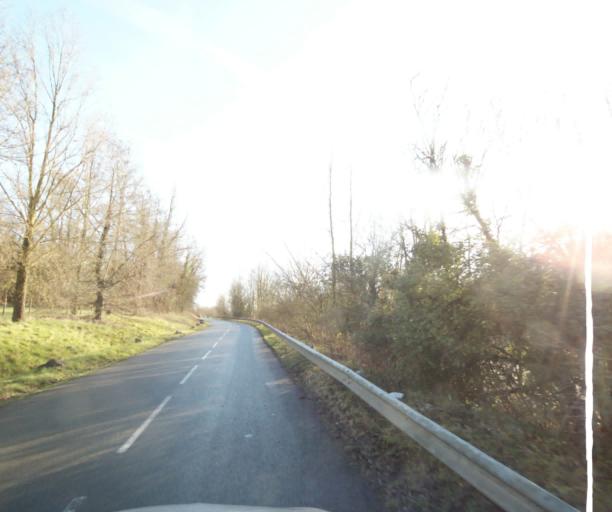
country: FR
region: Nord-Pas-de-Calais
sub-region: Departement du Nord
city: Curgies
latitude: 50.3281
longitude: 3.5948
